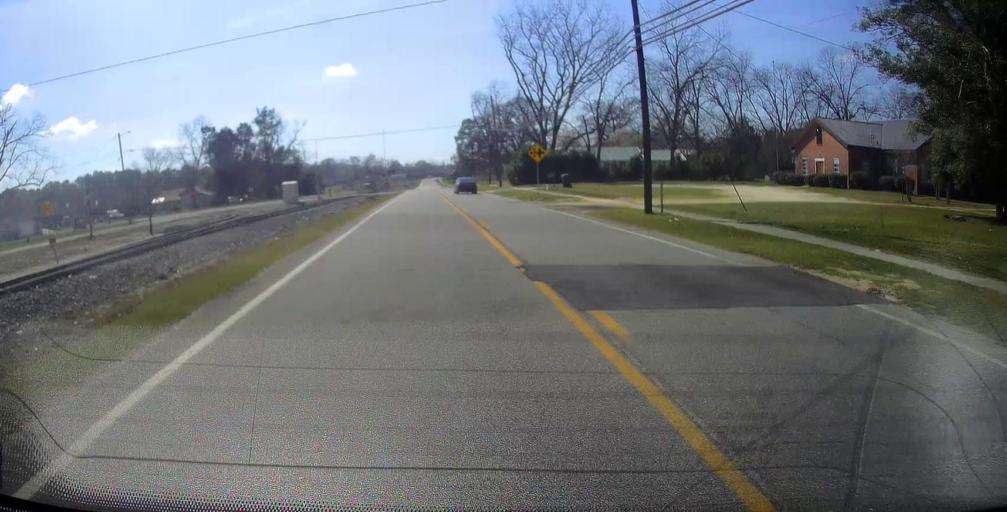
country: US
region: Georgia
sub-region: Wilkinson County
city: Gordon
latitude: 32.8843
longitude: -83.3243
